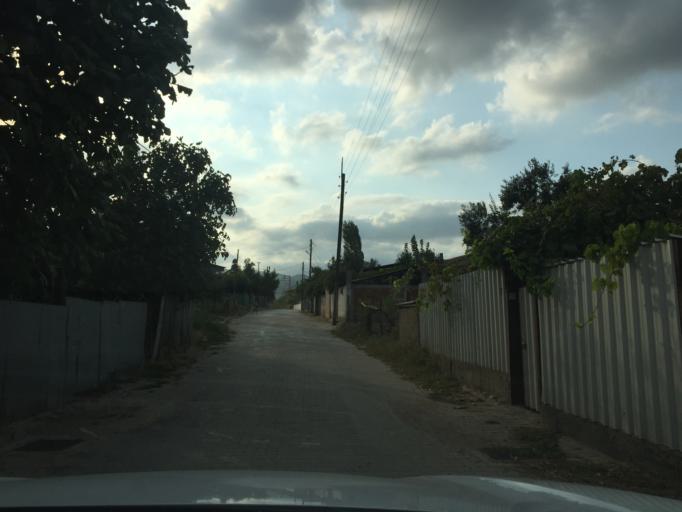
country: TR
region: Balikesir
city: Gonen
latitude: 40.0534
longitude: 27.5946
